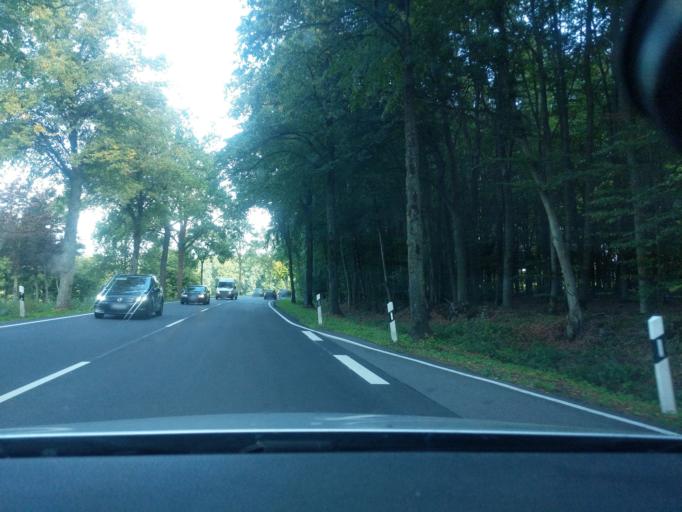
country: DE
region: Lower Saxony
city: Belm
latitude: 52.3310
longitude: 8.1688
